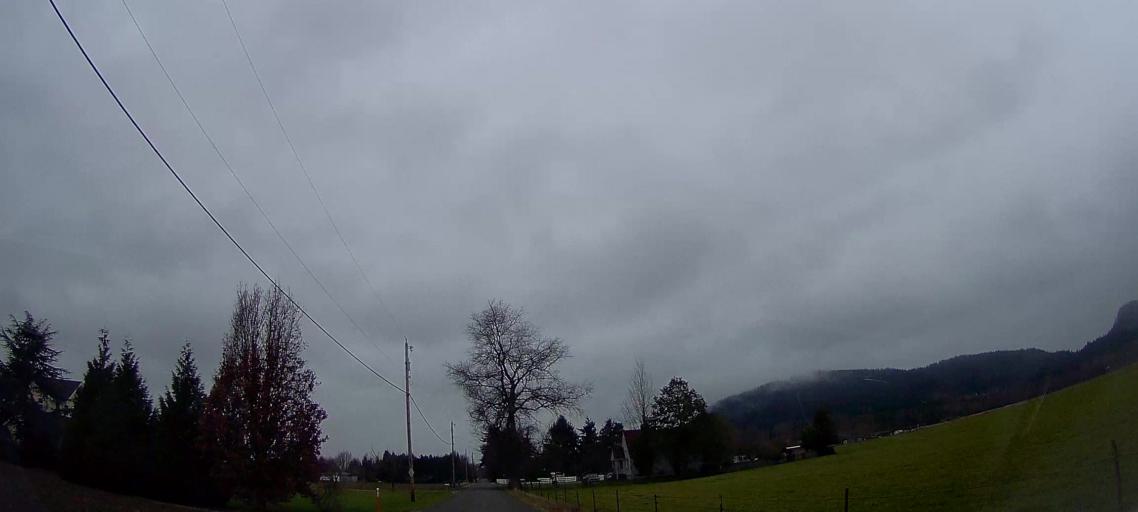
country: US
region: Washington
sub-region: Skagit County
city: Mount Vernon
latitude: 48.3740
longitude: -122.3241
